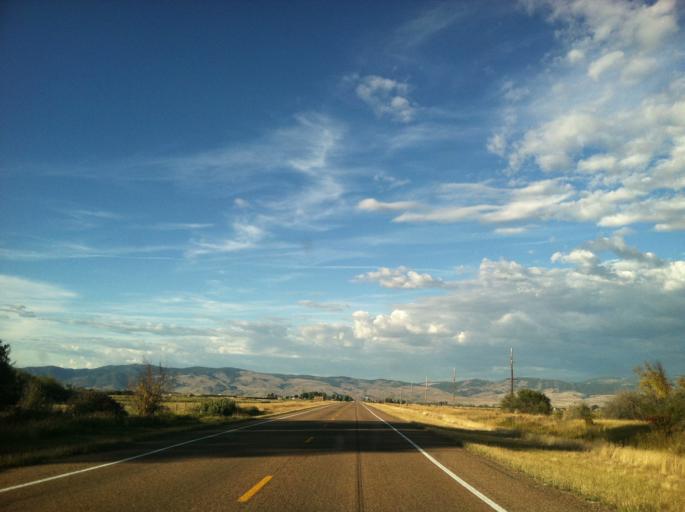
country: US
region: Montana
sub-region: Granite County
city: Philipsburg
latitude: 46.5691
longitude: -113.2076
